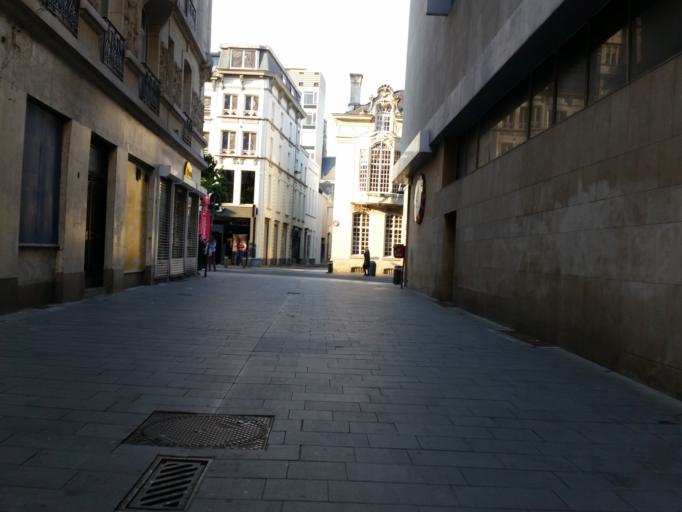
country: BE
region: Flanders
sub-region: Provincie Antwerpen
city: Antwerpen
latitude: 51.2176
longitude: 4.4103
